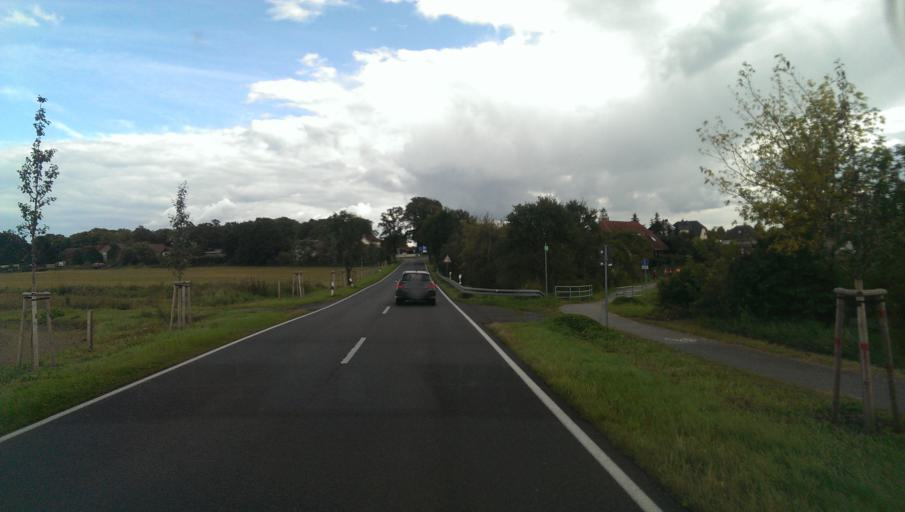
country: DE
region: Brandenburg
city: Velten
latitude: 52.6779
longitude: 13.1332
